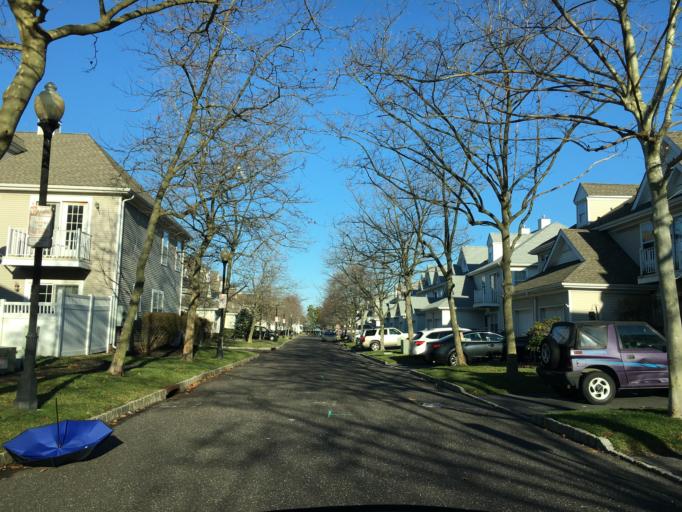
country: US
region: New Jersey
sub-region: Atlantic County
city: Atlantic City
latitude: 39.3739
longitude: -74.4173
